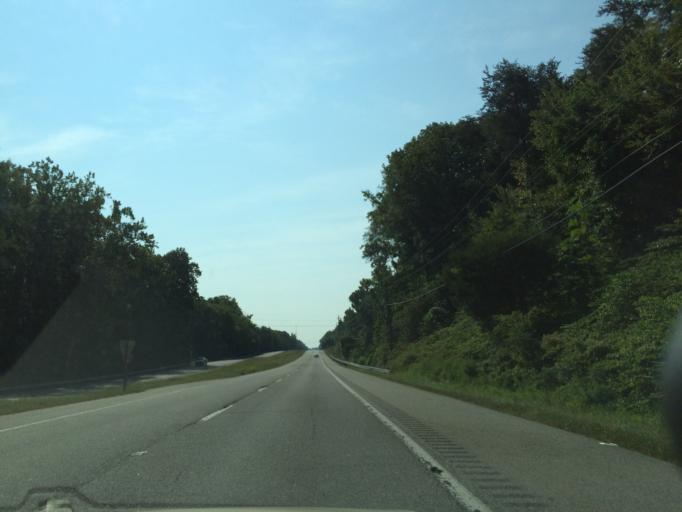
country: US
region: Maryland
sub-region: Charles County
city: La Plata
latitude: 38.4320
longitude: -76.9736
